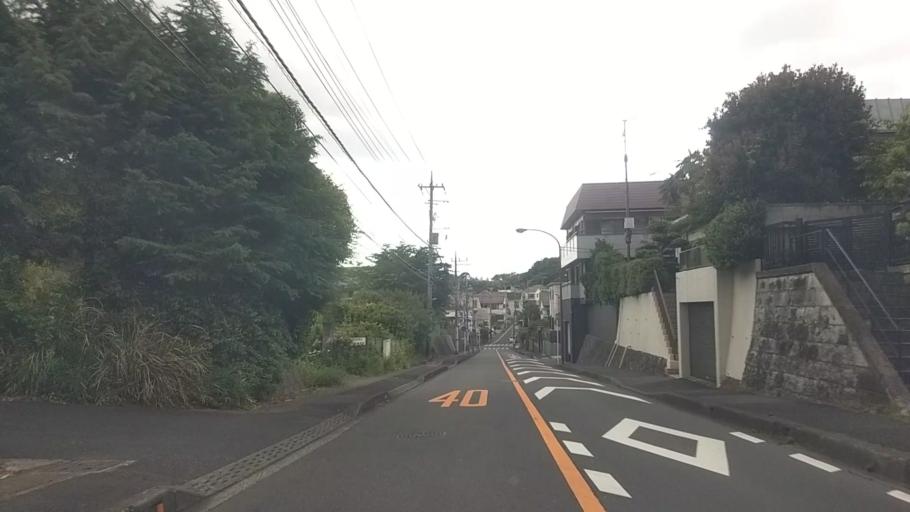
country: JP
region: Kanagawa
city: Fujisawa
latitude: 35.3570
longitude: 139.5203
